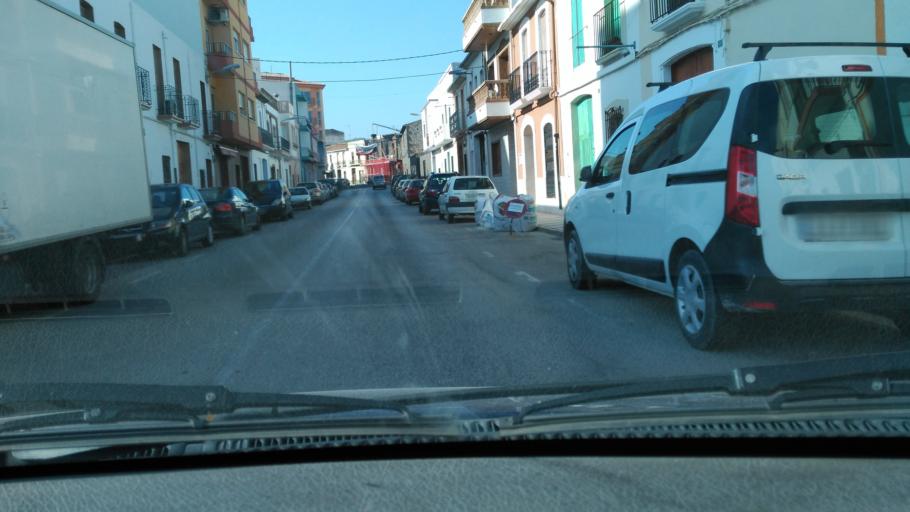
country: ES
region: Valencia
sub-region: Provincia de Alicante
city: Gata de Gorgos
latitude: 38.7777
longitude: 0.0850
